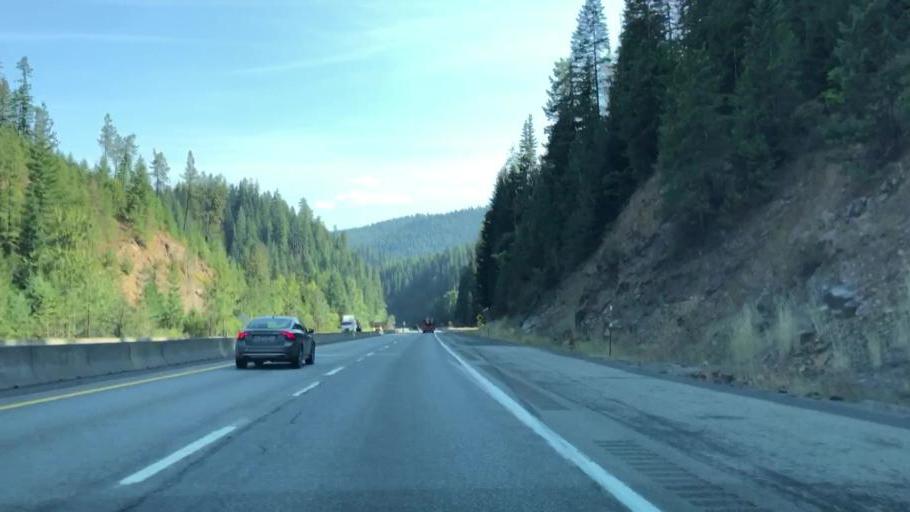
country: US
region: Idaho
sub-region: Shoshone County
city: Pinehurst
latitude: 47.6045
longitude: -116.5005
